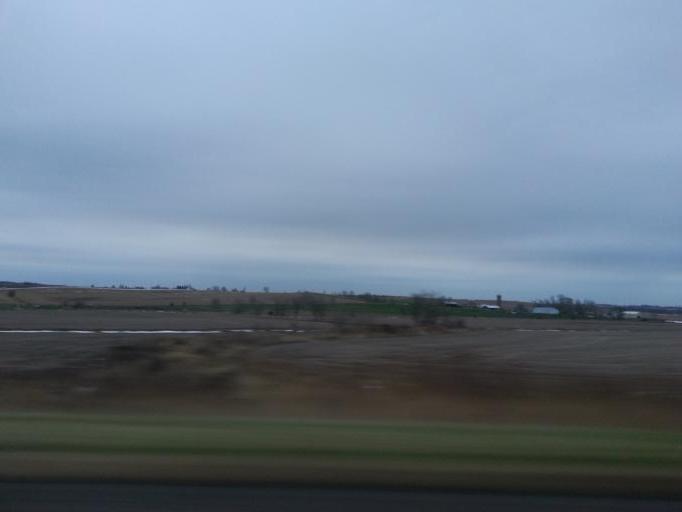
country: US
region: Iowa
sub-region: Benton County
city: Urbana
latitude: 42.2354
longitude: -91.8780
